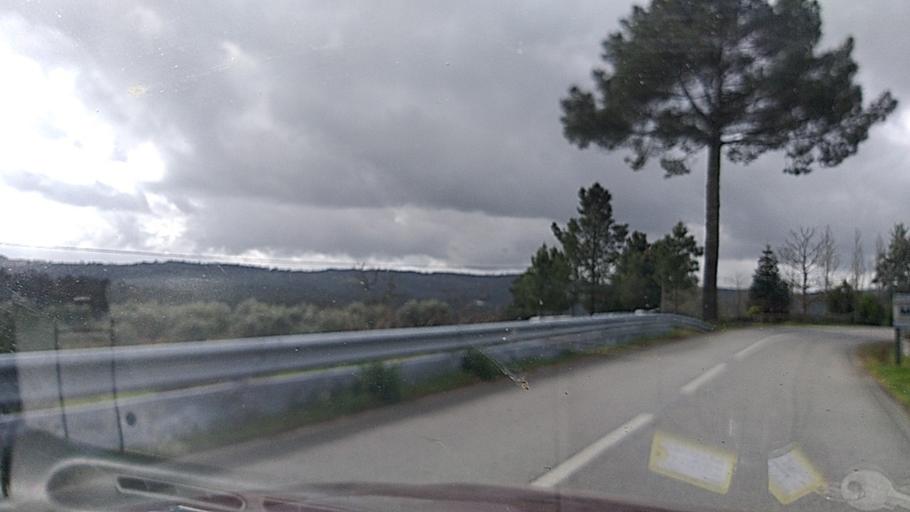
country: PT
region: Guarda
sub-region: Fornos de Algodres
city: Fornos de Algodres
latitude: 40.6598
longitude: -7.5778
